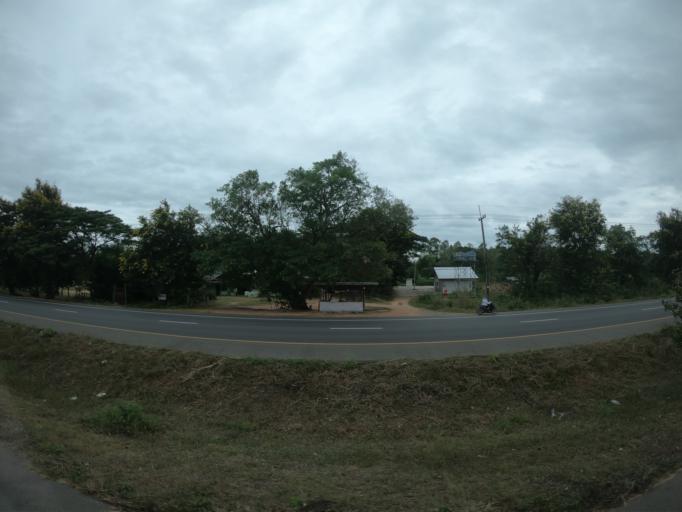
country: TH
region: Kalasin
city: Khong Chai
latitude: 16.1397
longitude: 103.4325
